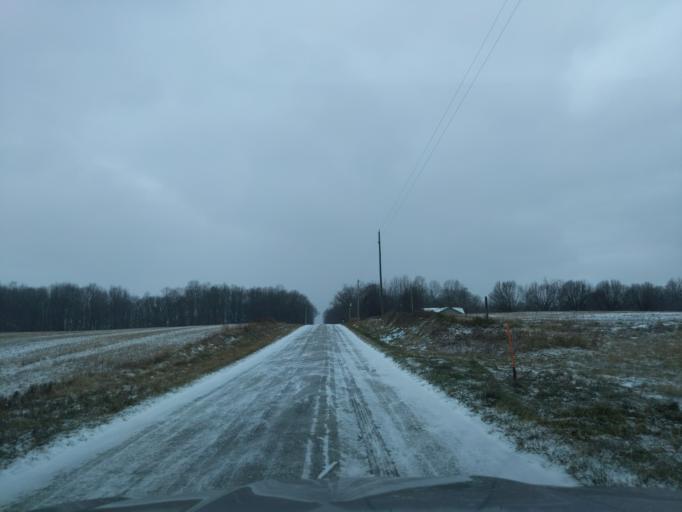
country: US
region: Indiana
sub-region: Decatur County
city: Greensburg
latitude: 39.2339
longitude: -85.4833
